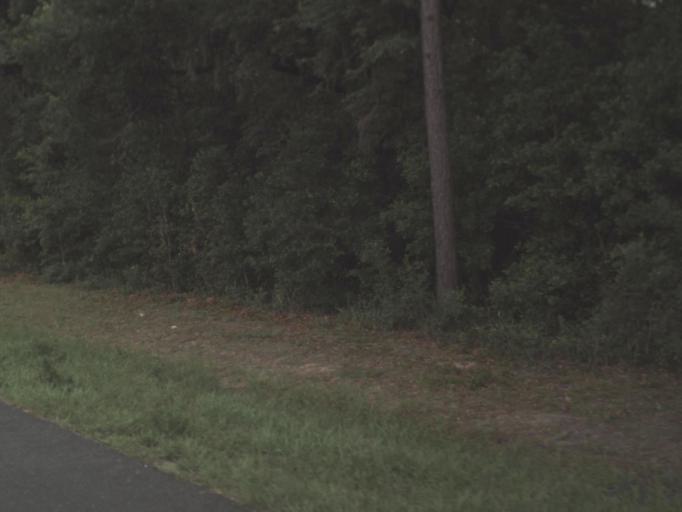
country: US
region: Florida
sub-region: Levy County
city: Williston Highlands
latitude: 29.2407
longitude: -82.4413
